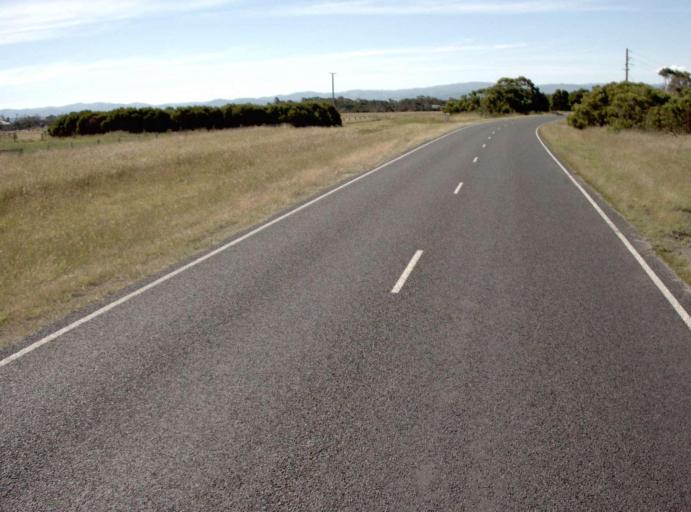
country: AU
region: Victoria
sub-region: Latrobe
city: Traralgon
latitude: -38.6259
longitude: 146.6749
